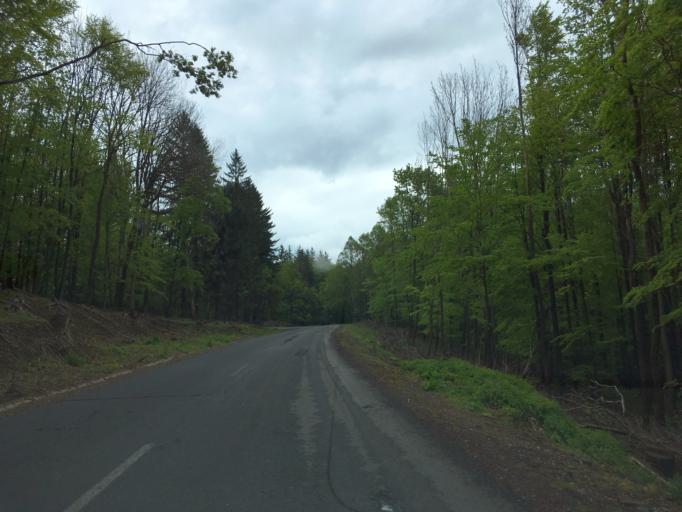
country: HU
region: Nograd
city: Batonyterenye
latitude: 47.9120
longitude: 19.8940
